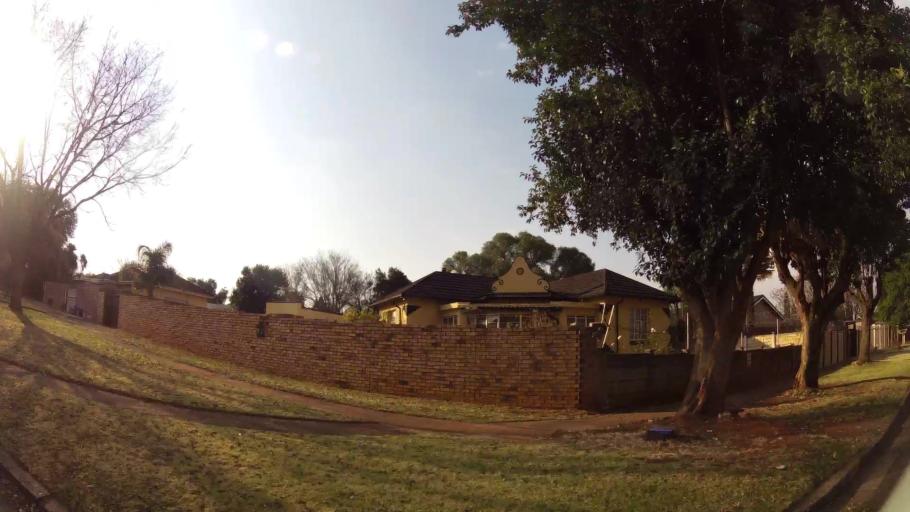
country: ZA
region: Gauteng
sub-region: Ekurhuleni Metropolitan Municipality
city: Springs
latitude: -26.2781
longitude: 28.4477
